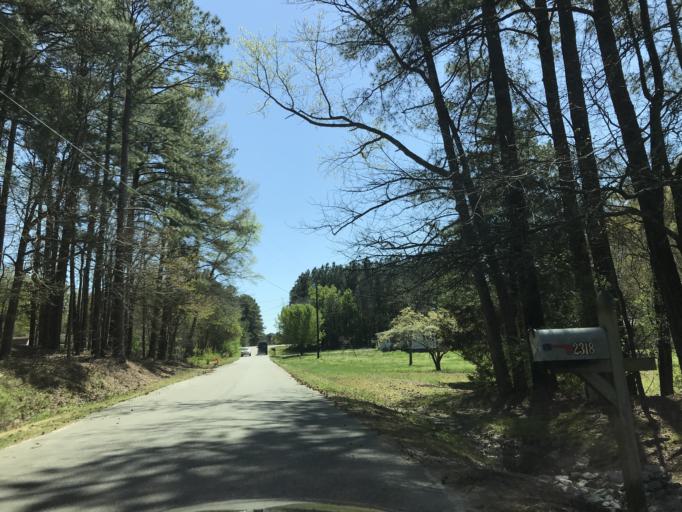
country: US
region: North Carolina
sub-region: Wake County
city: Raleigh
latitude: 35.8121
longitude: -78.5764
